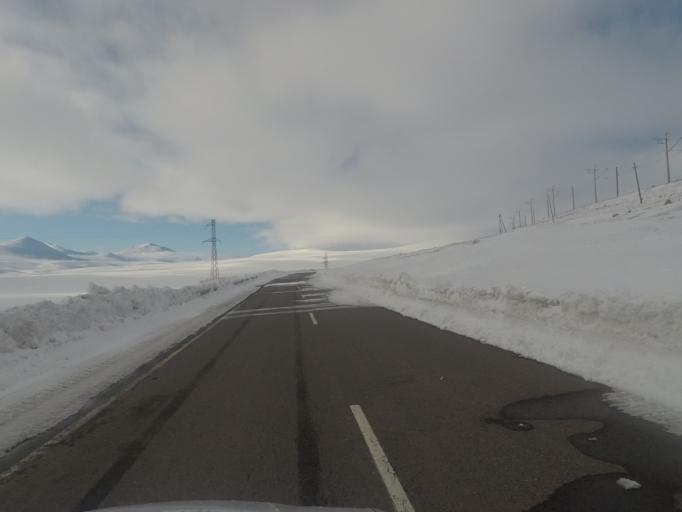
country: GE
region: Kvemo Kartli
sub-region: Tsalka
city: Tsalka
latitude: 41.4749
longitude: 43.8514
